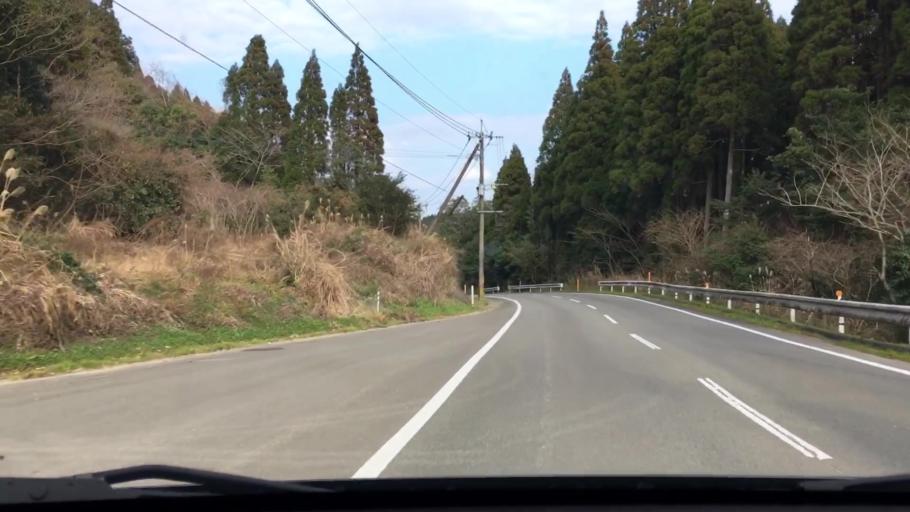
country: JP
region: Miyazaki
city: Kushima
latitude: 31.5771
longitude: 131.2701
